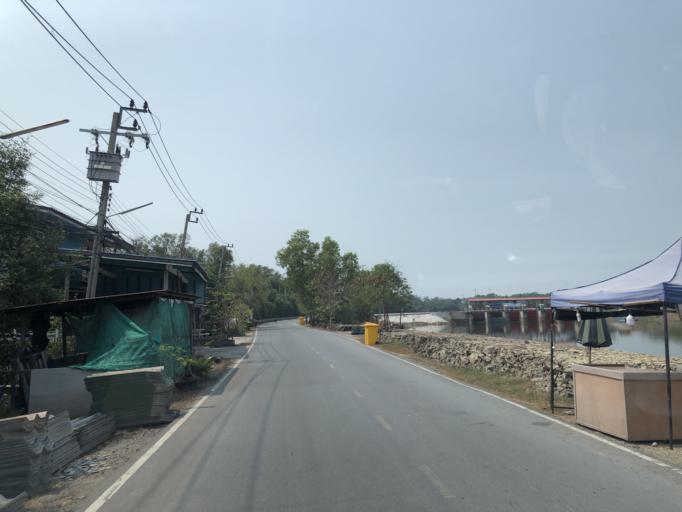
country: TH
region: Samut Prakan
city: Bang Bo
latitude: 13.5171
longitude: 100.8239
